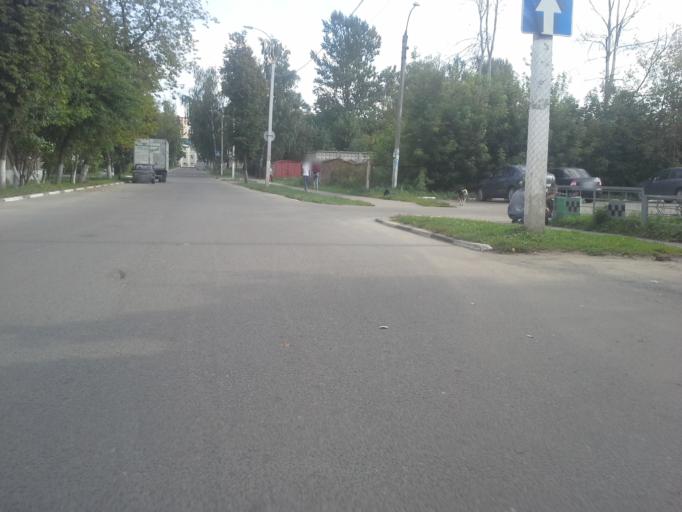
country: RU
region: Moskovskaya
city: Aprelevka
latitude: 55.5502
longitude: 37.0777
